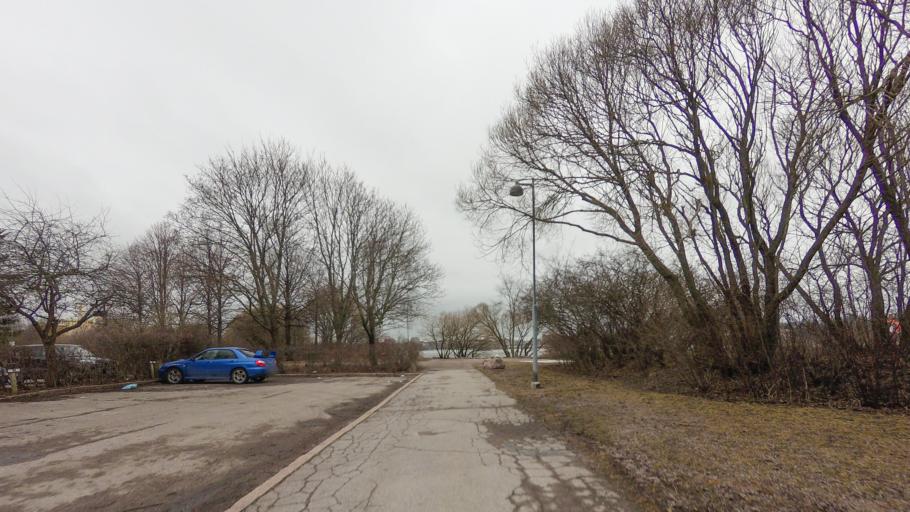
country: FI
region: Uusimaa
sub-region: Helsinki
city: Helsinki
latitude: 60.1687
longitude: 24.9777
